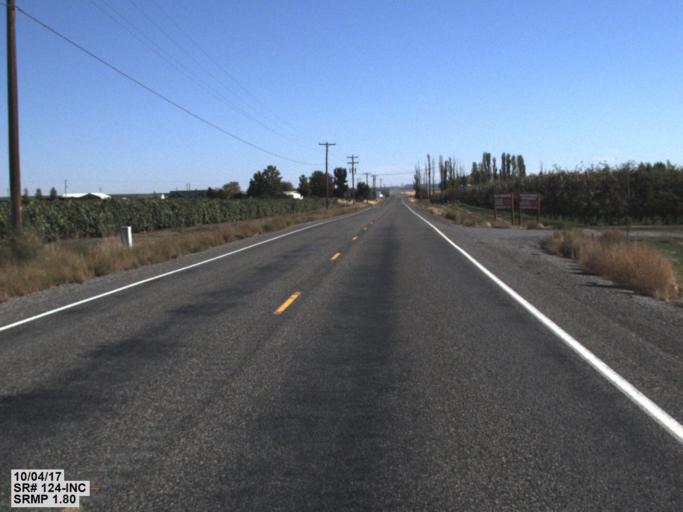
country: US
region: Washington
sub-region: Walla Walla County
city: Burbank
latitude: 46.2117
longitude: -118.9771
